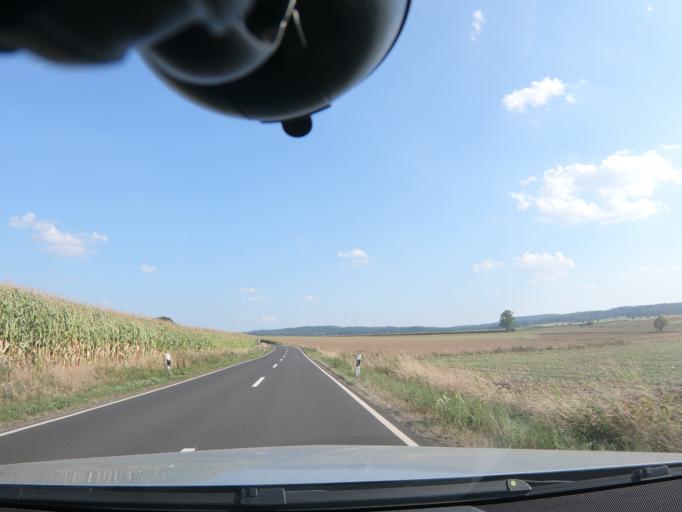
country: DE
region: Hesse
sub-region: Regierungsbezirk Giessen
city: Ebsdorfergrund
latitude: 50.7762
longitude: 8.8643
